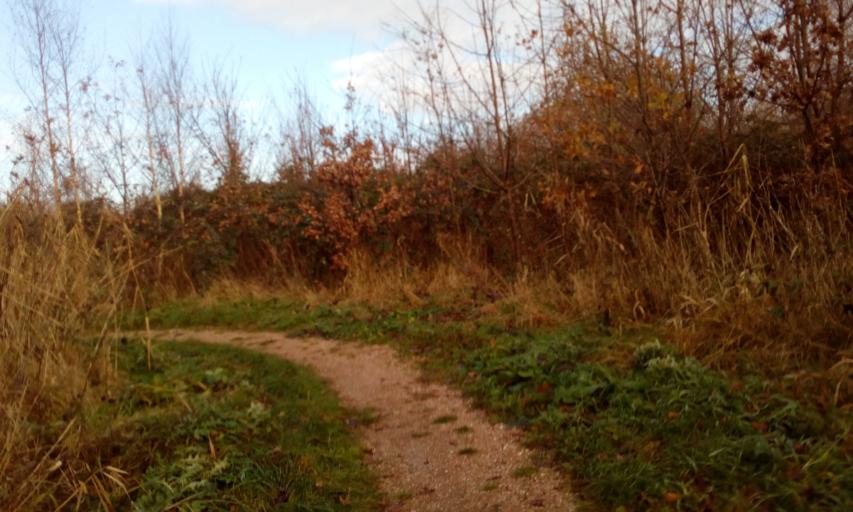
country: NL
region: South Holland
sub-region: Gemeente Lansingerland
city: Bergschenhoek
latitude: 51.9738
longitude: 4.5034
